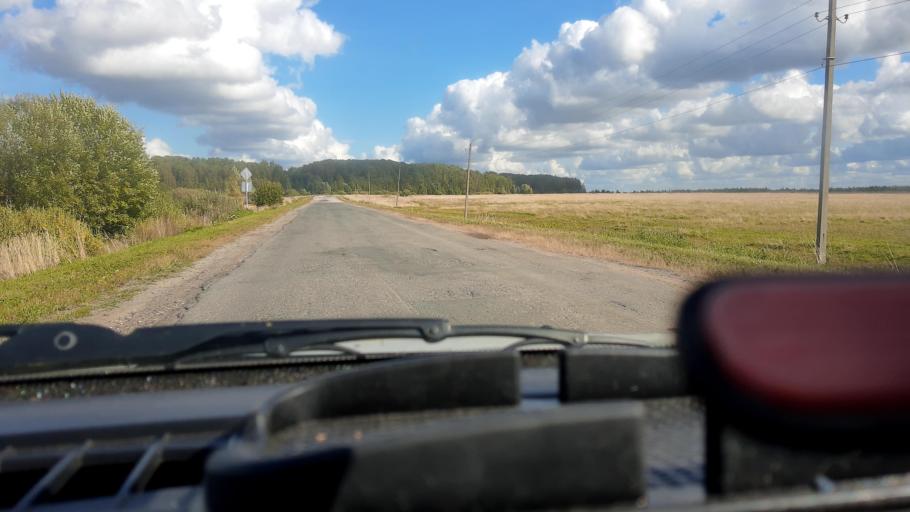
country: RU
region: Nizjnij Novgorod
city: Sharanga
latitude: 56.9387
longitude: 46.6548
